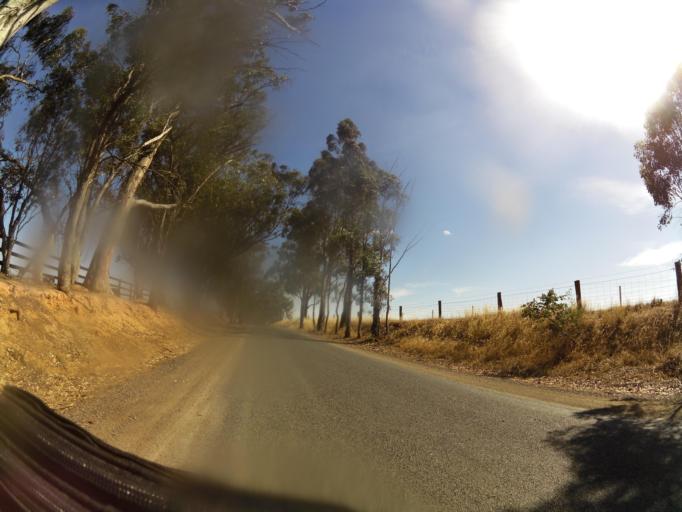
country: AU
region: Victoria
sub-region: Campaspe
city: Kyabram
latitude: -36.8598
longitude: 145.0883
